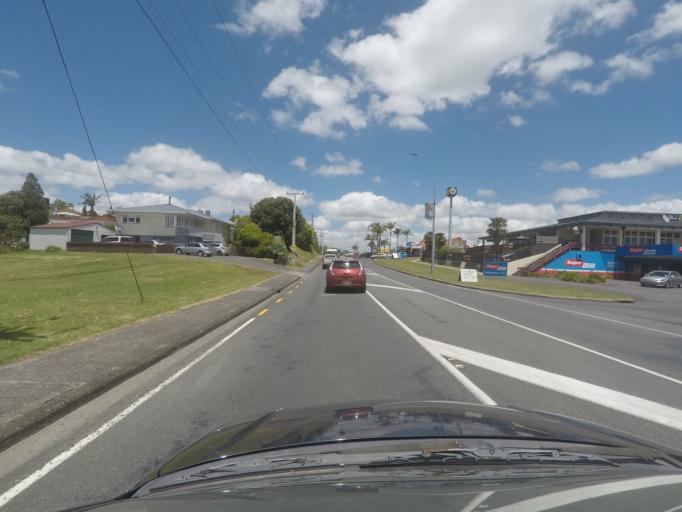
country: NZ
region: Northland
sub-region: Whangarei
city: Whangarei
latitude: -35.7535
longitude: 174.3683
